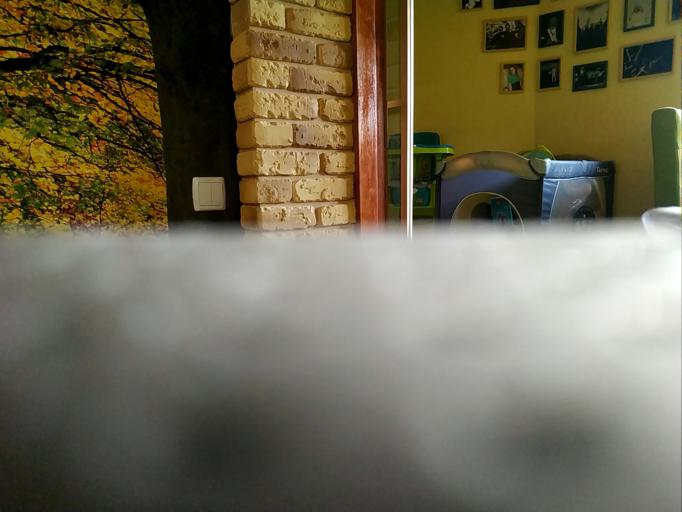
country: RU
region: Kaluga
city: Seredeyskiy
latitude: 54.0365
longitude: 35.3036
